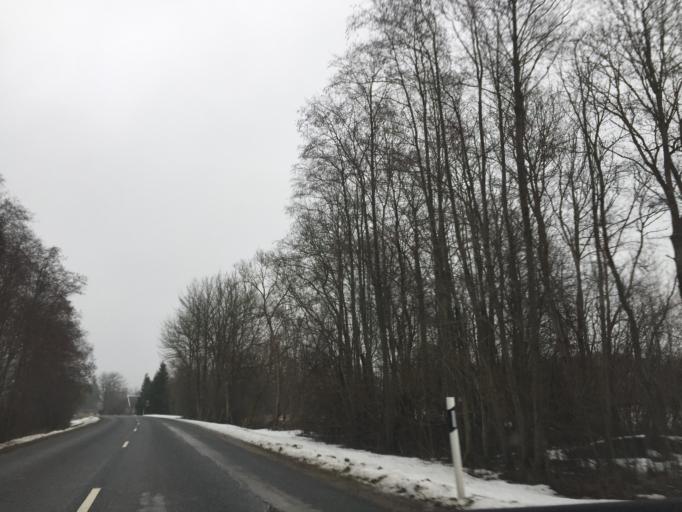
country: EE
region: Saare
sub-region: Kuressaare linn
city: Kuressaare
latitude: 58.3543
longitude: 22.8056
